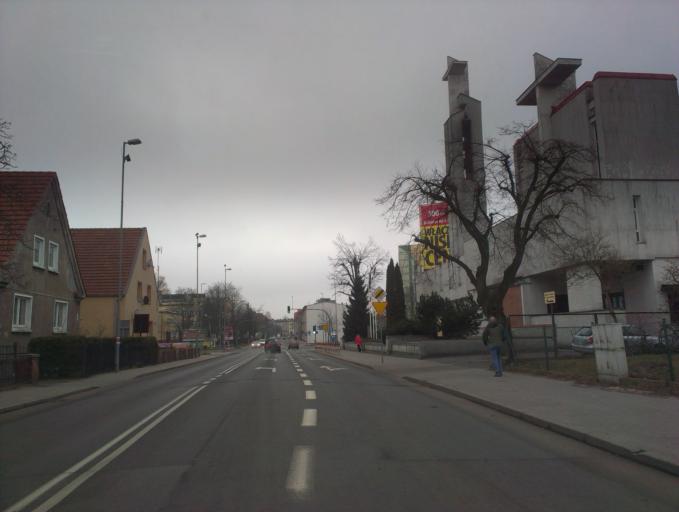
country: PL
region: West Pomeranian Voivodeship
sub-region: Koszalin
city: Koszalin
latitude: 54.1970
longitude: 16.1730
